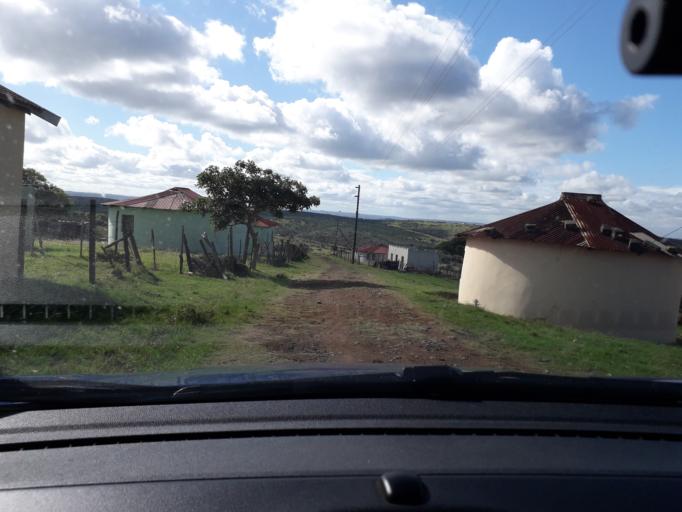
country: ZA
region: Eastern Cape
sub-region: Buffalo City Metropolitan Municipality
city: Bhisho
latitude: -33.1098
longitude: 27.4288
